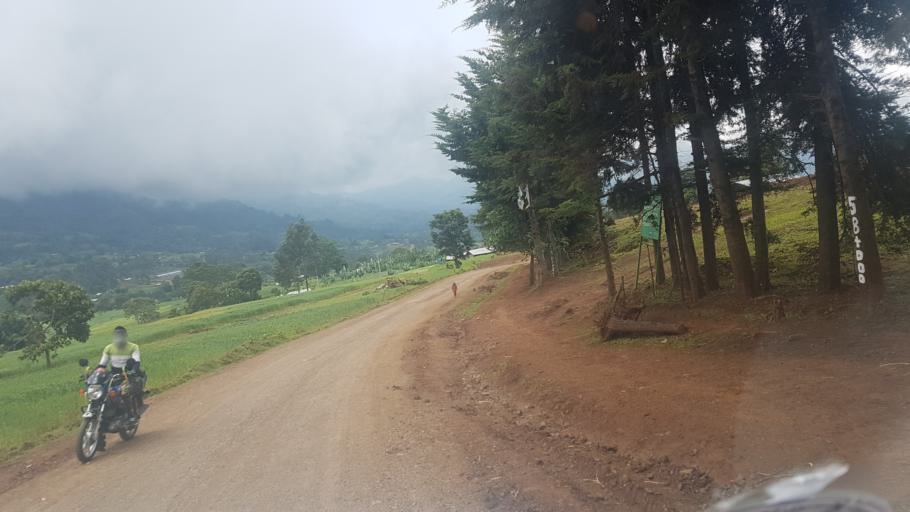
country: ET
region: Southern Nations, Nationalities, and People's Region
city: Arba Minch'
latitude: 6.3191
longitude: 37.5347
